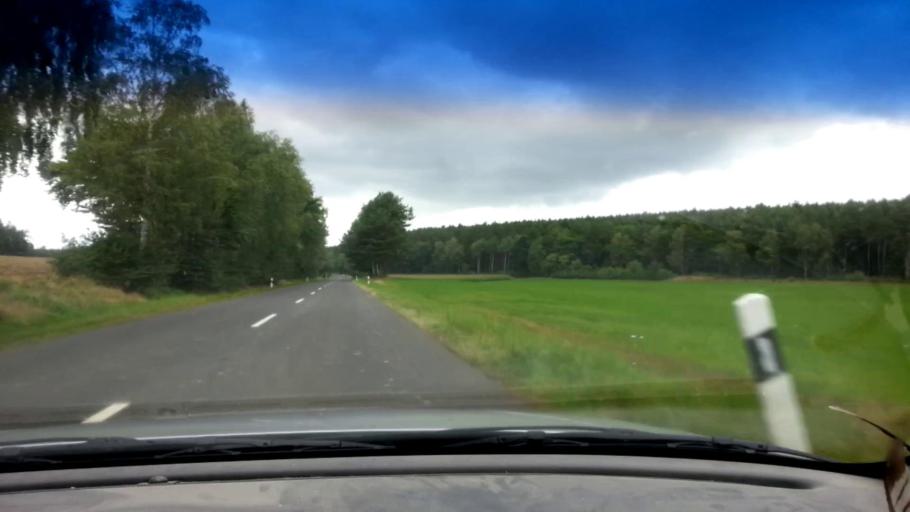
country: DE
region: Bavaria
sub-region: Upper Palatinate
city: Waldsassen
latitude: 50.0304
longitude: 12.3152
